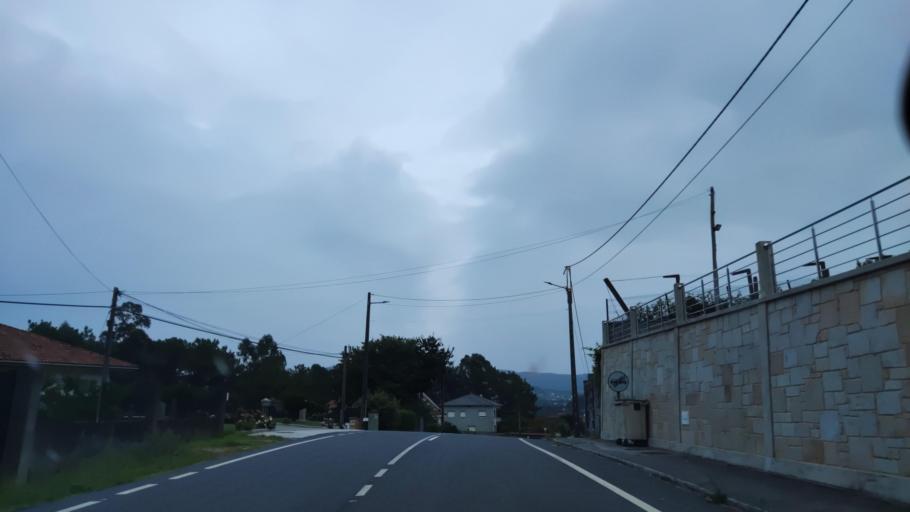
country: ES
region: Galicia
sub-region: Provincia de Pontevedra
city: Catoira
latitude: 42.6821
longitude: -8.7331
